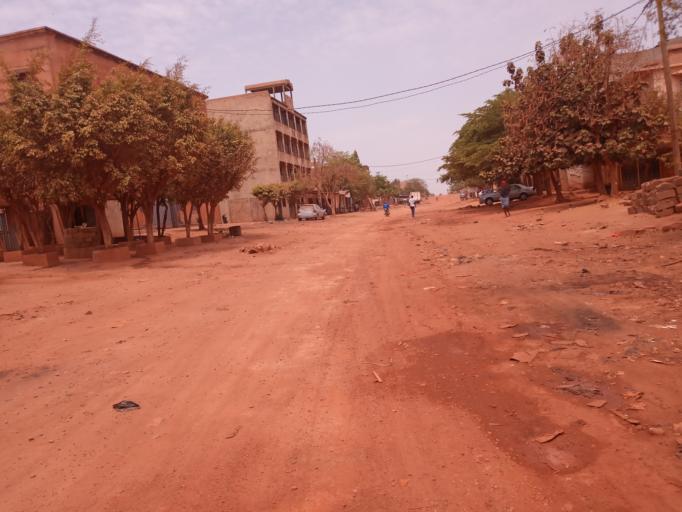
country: ML
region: Bamako
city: Bamako
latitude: 12.5577
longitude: -7.9816
